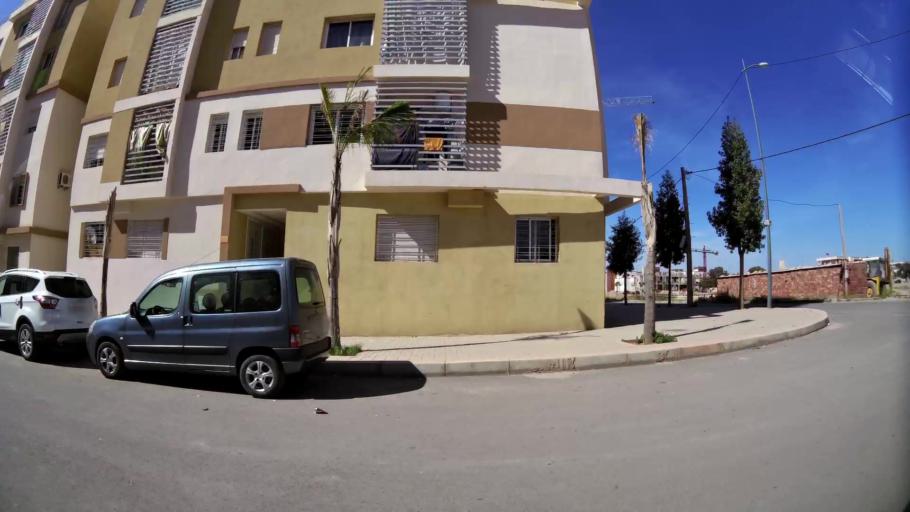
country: MA
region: Oriental
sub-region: Oujda-Angad
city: Oujda
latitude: 34.6625
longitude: -1.9137
